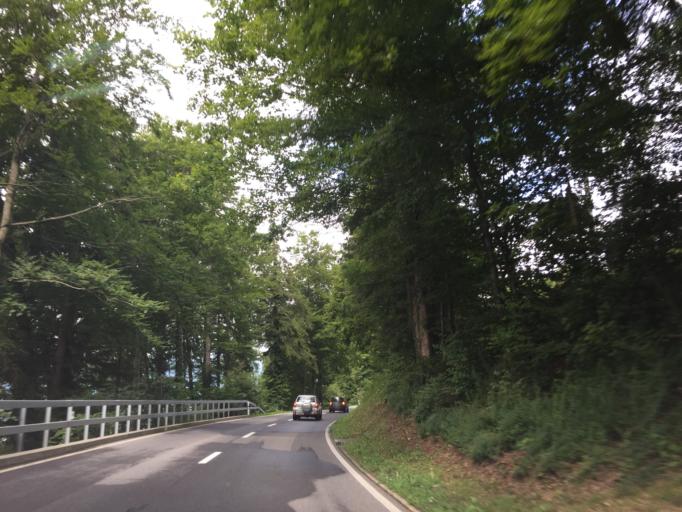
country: CH
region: Obwalden
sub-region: Obwalden
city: Kerns
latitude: 46.8679
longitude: 8.2761
